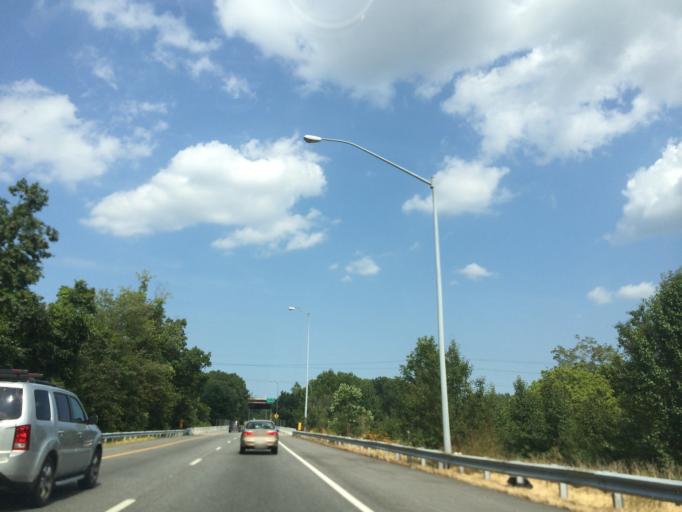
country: US
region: Maryland
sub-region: Howard County
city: Elkridge
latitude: 39.1990
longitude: -76.6992
